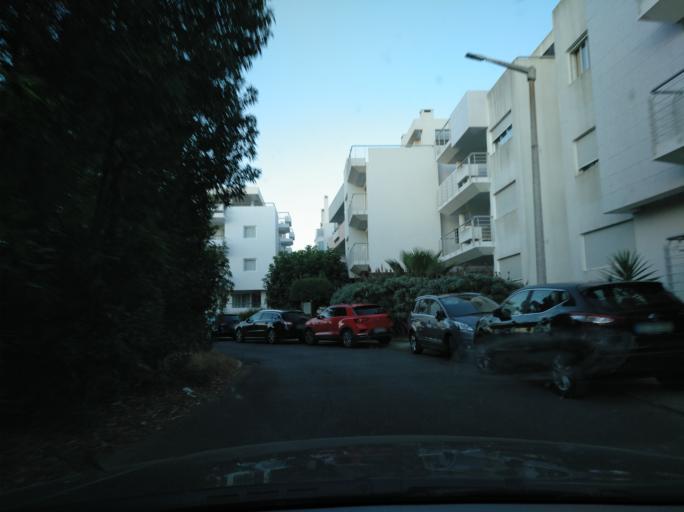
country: PT
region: Faro
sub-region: Tavira
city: Tavira
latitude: 37.1330
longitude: -7.6083
